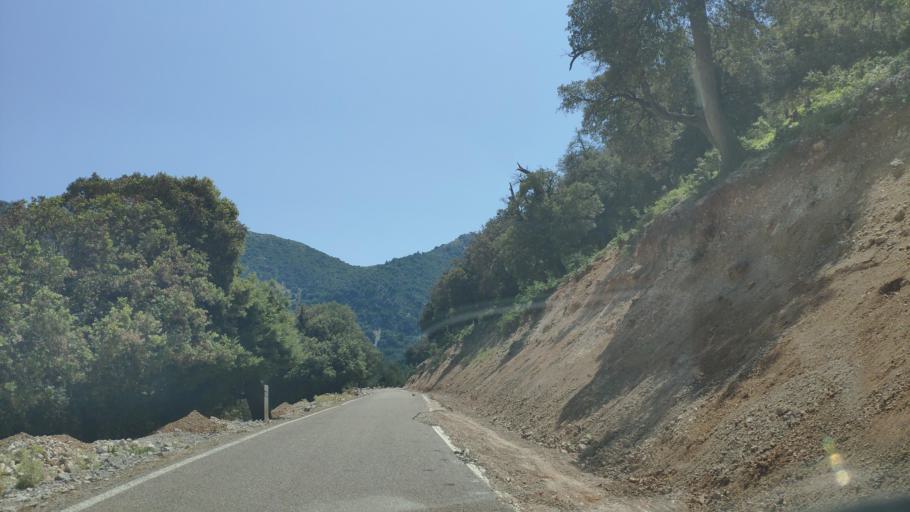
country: GR
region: West Greece
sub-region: Nomos Aitolias kai Akarnanias
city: Krikellos
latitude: 39.0186
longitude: 21.3460
